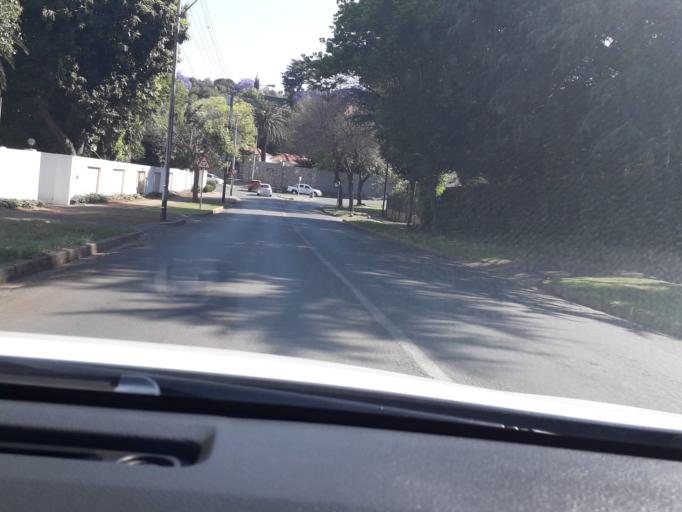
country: ZA
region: Gauteng
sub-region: City of Johannesburg Metropolitan Municipality
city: Johannesburg
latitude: -26.1797
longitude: 28.0212
